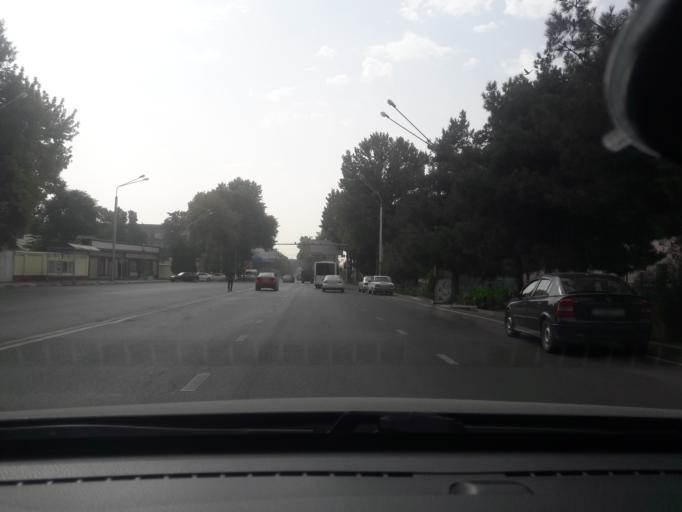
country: TJ
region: Dushanbe
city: Dushanbe
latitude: 38.5764
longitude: 68.8037
